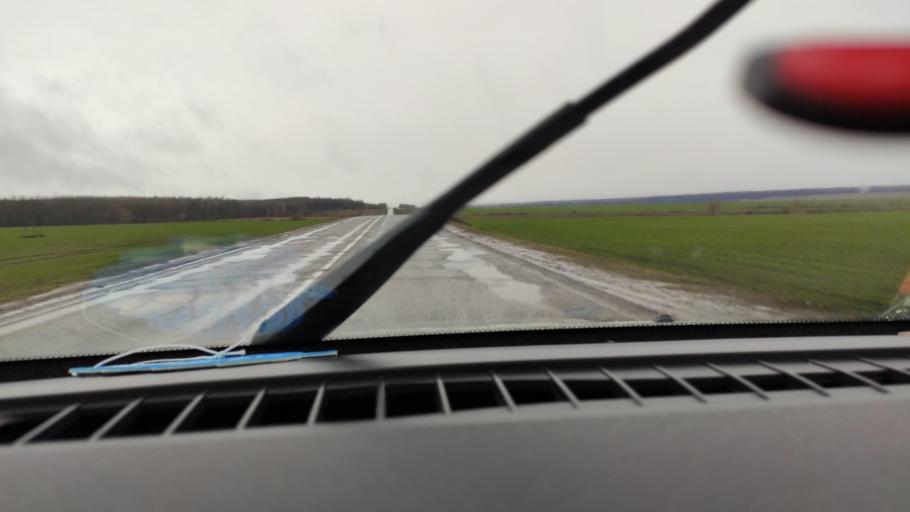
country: RU
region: Samara
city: Chelno-Vershiny
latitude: 54.6316
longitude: 50.9647
